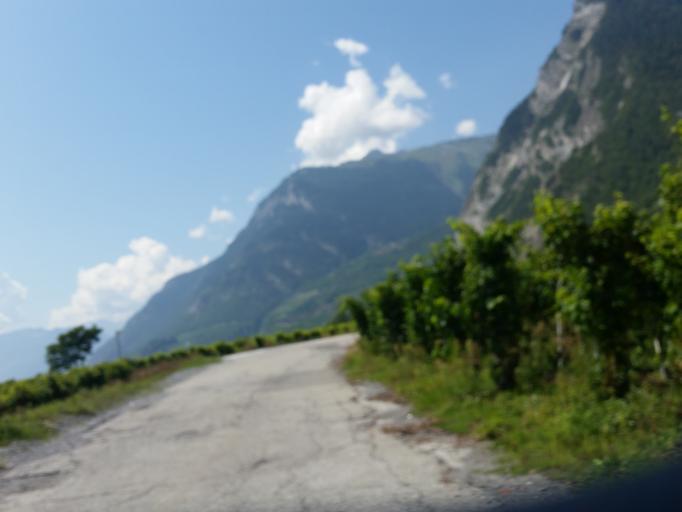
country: CH
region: Valais
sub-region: Conthey District
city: Chamoson
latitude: 46.1944
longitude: 7.2289
